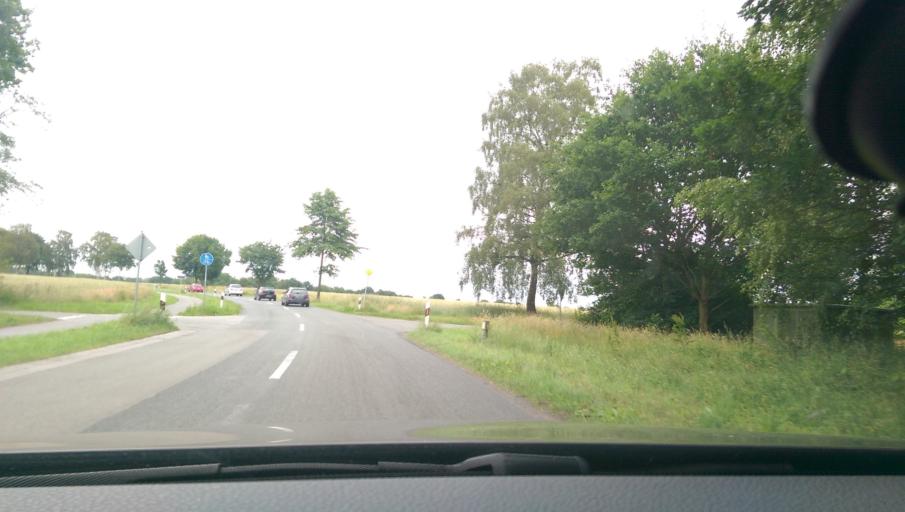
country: DE
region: Lower Saxony
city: Horstedt
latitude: 53.1758
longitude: 9.2670
